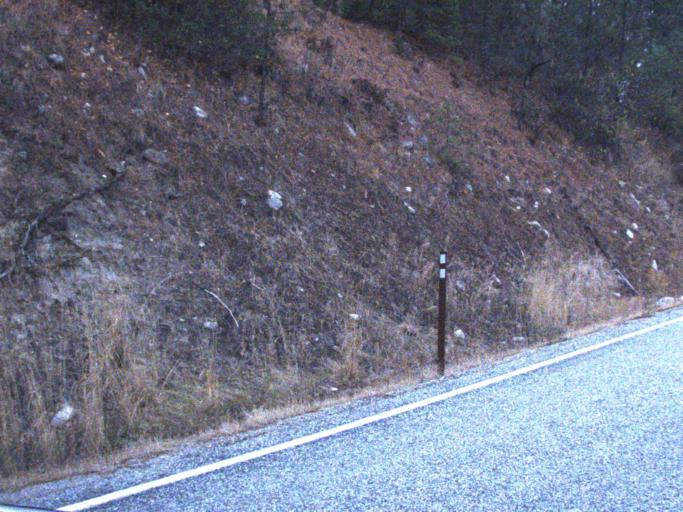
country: CA
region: British Columbia
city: Grand Forks
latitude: 48.9556
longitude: -118.2143
